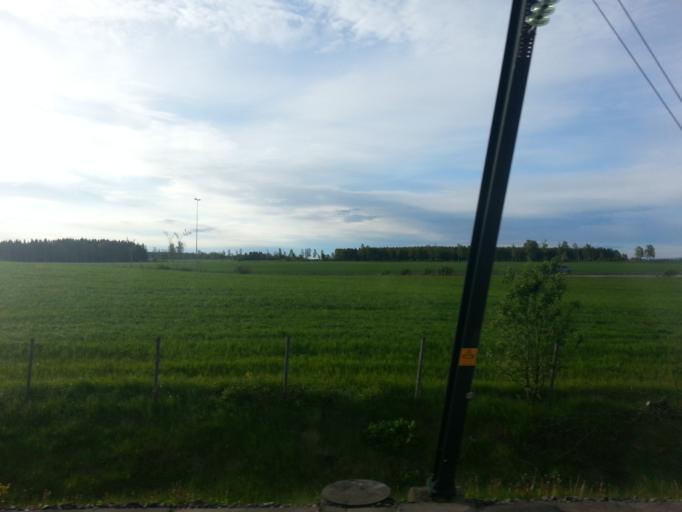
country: NO
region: Akershus
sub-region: Ullensaker
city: Jessheim
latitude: 60.1146
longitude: 11.1523
